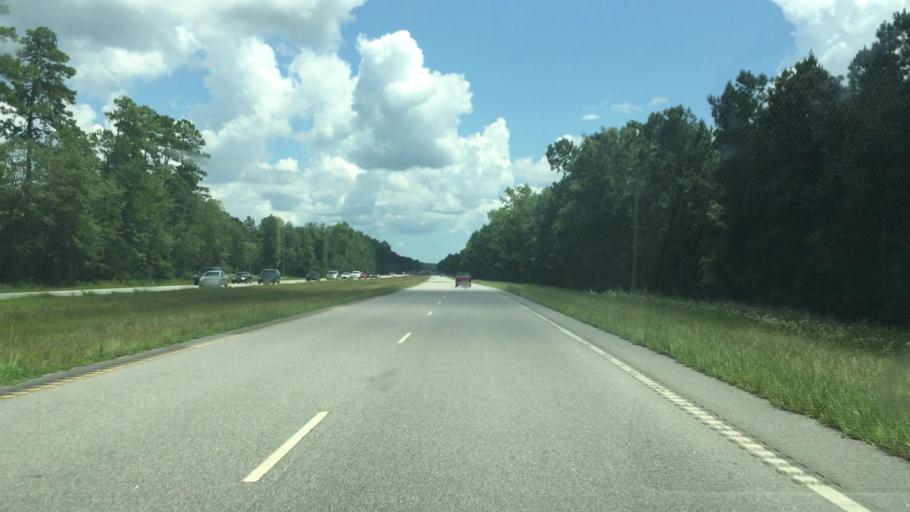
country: US
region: South Carolina
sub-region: Horry County
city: Loris
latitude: 34.0456
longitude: -78.8306
